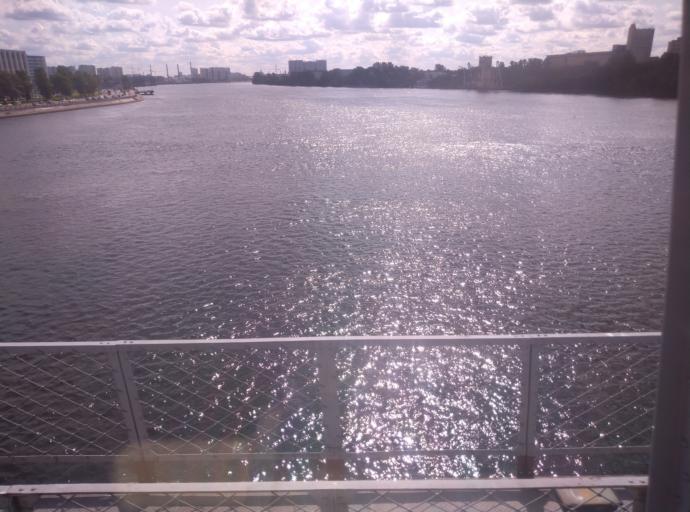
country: RU
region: St.-Petersburg
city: Centralniy
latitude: 59.9156
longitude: 30.4107
